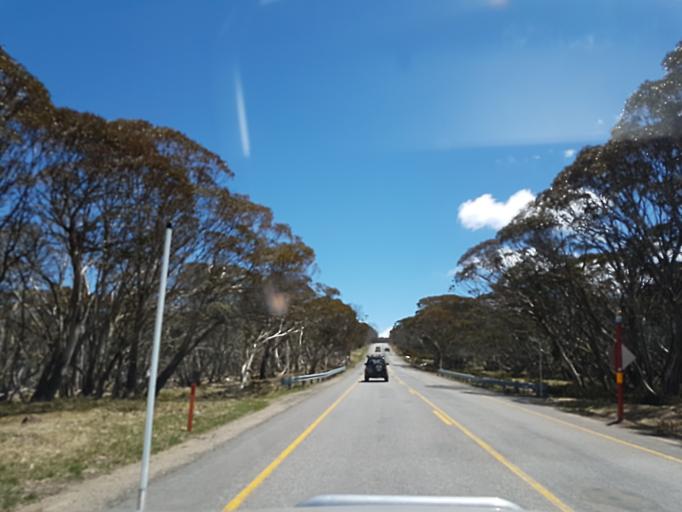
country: AU
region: Victoria
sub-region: Alpine
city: Mount Beauty
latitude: -37.0041
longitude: 147.1832
